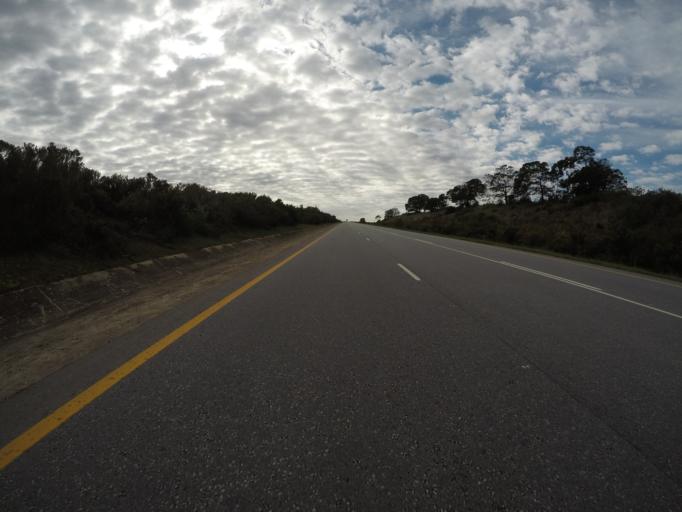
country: ZA
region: Eastern Cape
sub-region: Cacadu District Municipality
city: Kruisfontein
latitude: -34.0065
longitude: 24.6712
